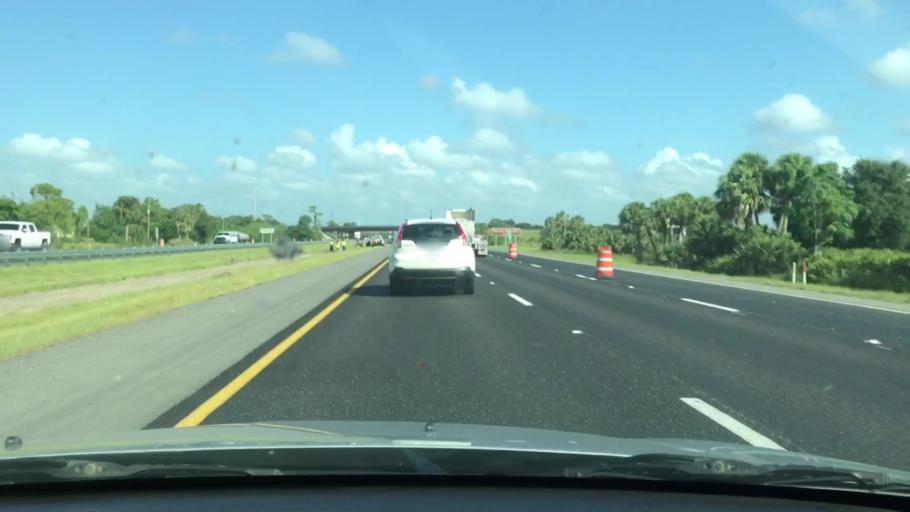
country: US
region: Florida
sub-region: Charlotte County
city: Punta Gorda
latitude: 26.9235
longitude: -82.0137
